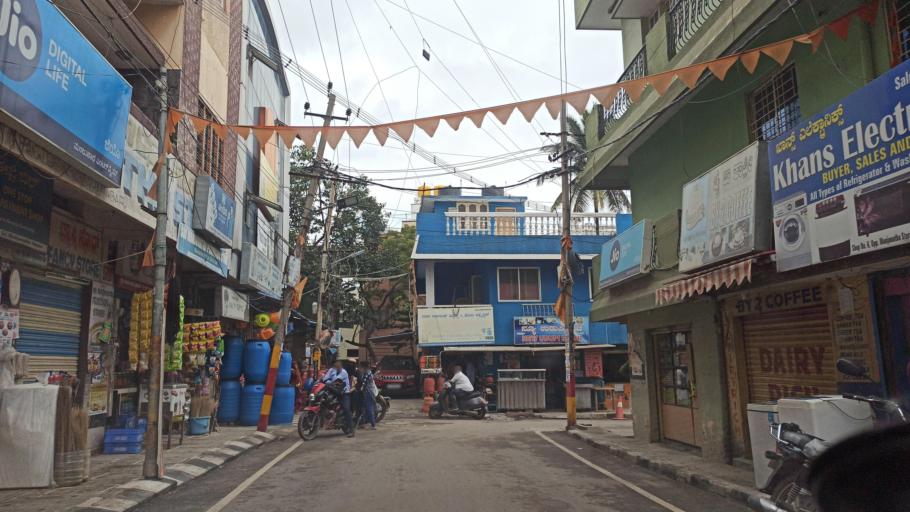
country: IN
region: Karnataka
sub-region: Bangalore Urban
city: Bangalore
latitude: 12.9935
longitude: 77.6732
